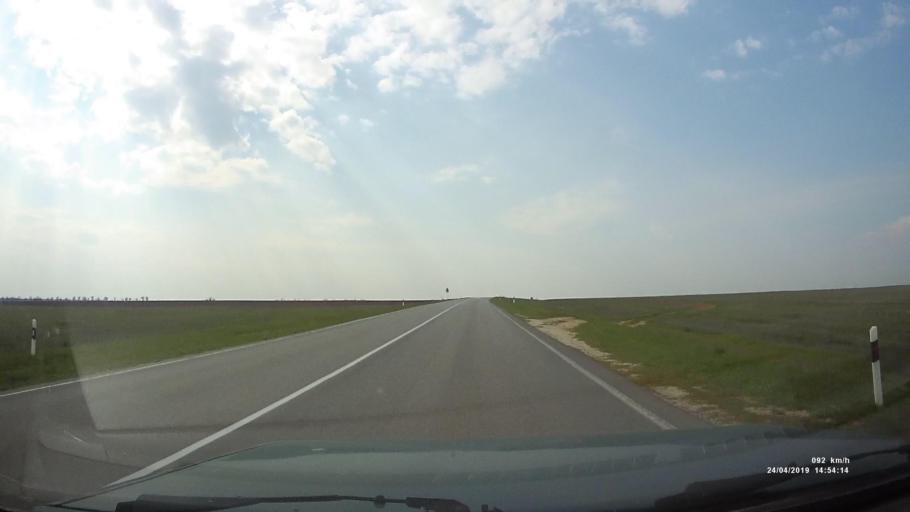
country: RU
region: Rostov
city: Remontnoye
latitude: 46.5331
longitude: 43.6426
